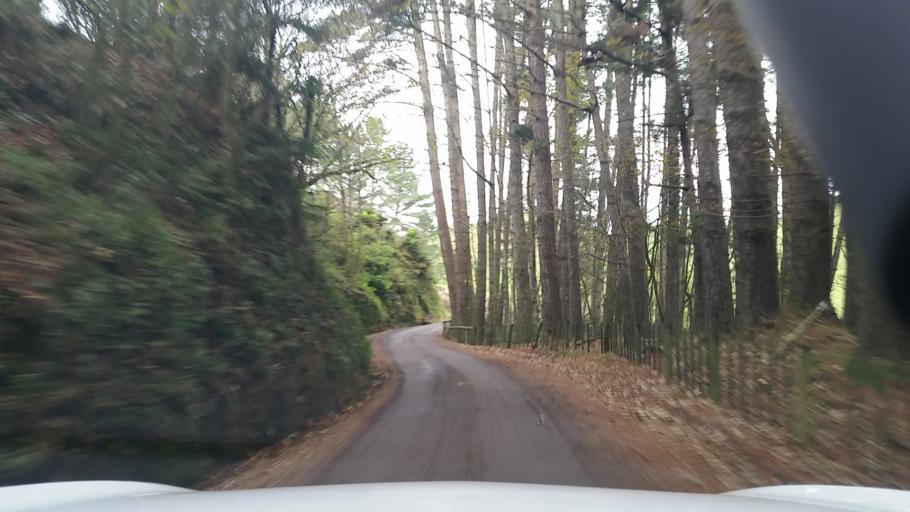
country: NZ
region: Taranaki
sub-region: New Plymouth District
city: Waitara
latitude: -39.1500
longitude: 174.5101
